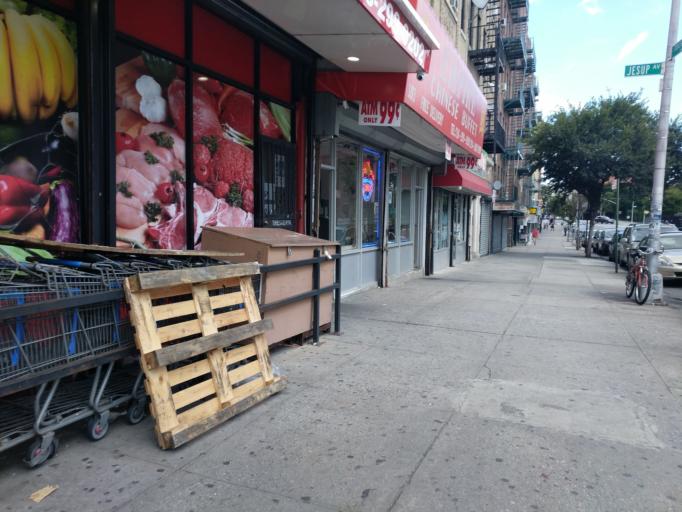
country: US
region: New York
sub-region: New York County
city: Inwood
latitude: 40.8463
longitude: -73.9185
